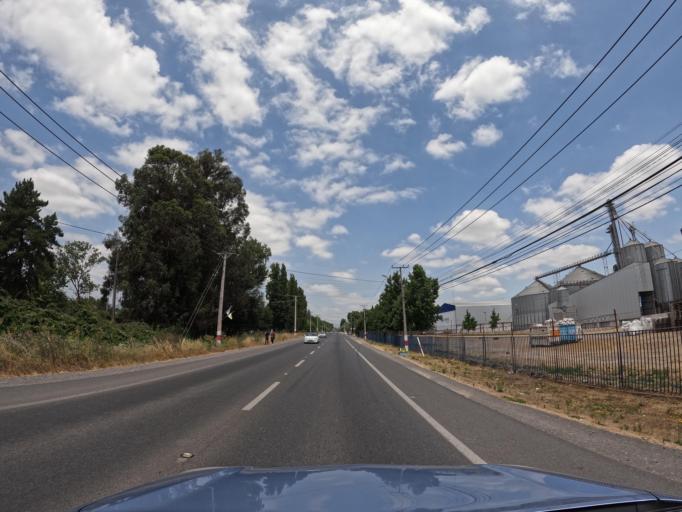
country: CL
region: Maule
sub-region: Provincia de Curico
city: Curico
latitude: -35.0059
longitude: -71.2237
